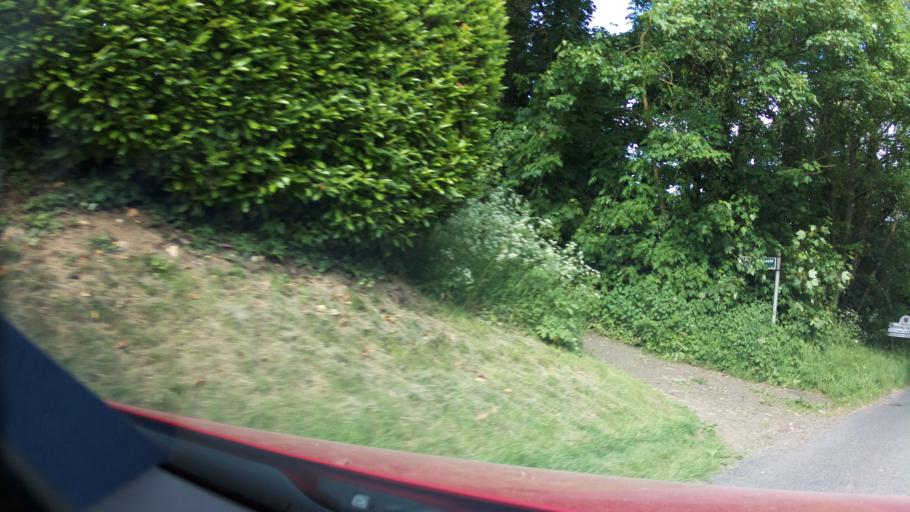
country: GB
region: England
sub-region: Gloucestershire
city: Chipping Campden
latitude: 52.0498
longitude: -1.7935
